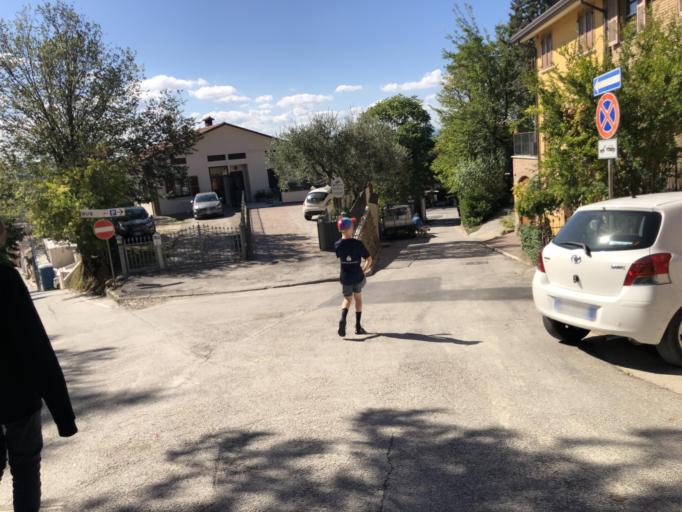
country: IT
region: The Marches
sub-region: Provincia di Pesaro e Urbino
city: Gradara
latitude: 43.9408
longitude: 12.7728
